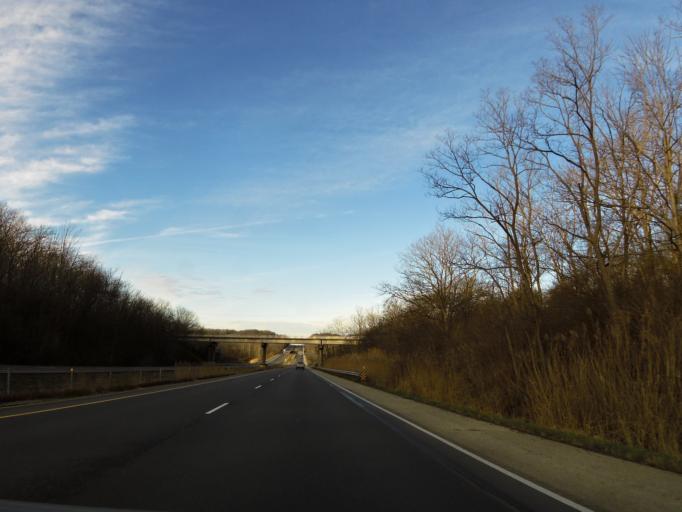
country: US
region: Illinois
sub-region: Vermilion County
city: Oakwood
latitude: 40.1277
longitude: -87.7261
